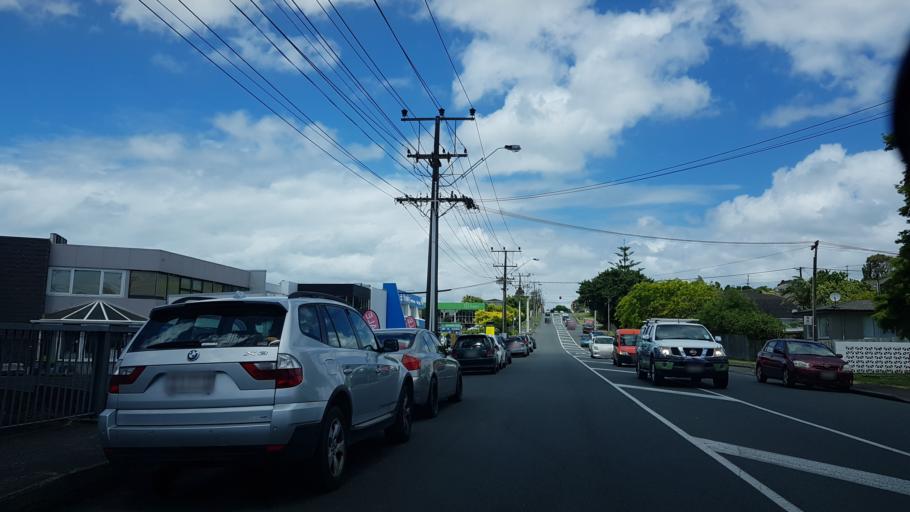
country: NZ
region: Auckland
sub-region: Auckland
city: North Shore
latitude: -36.7848
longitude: 174.7396
